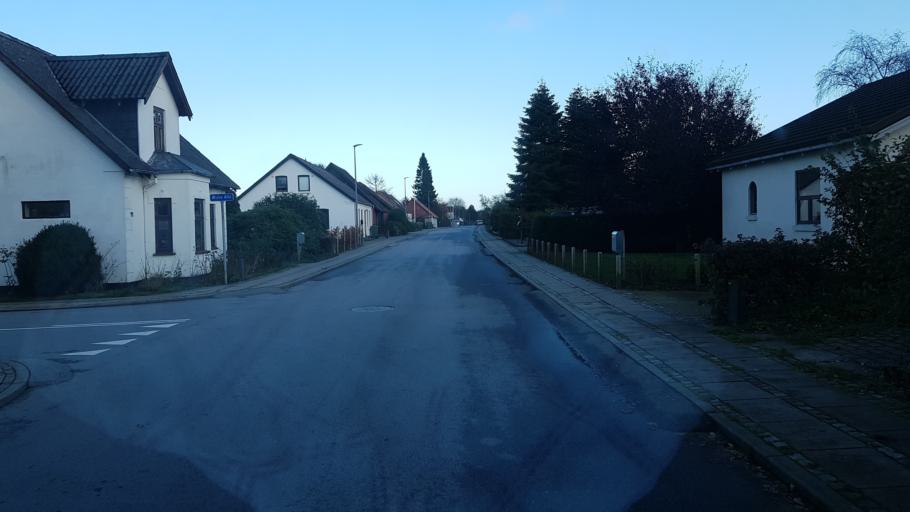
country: DK
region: South Denmark
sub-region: Vejen Kommune
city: Holsted
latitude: 55.4834
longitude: 8.9144
